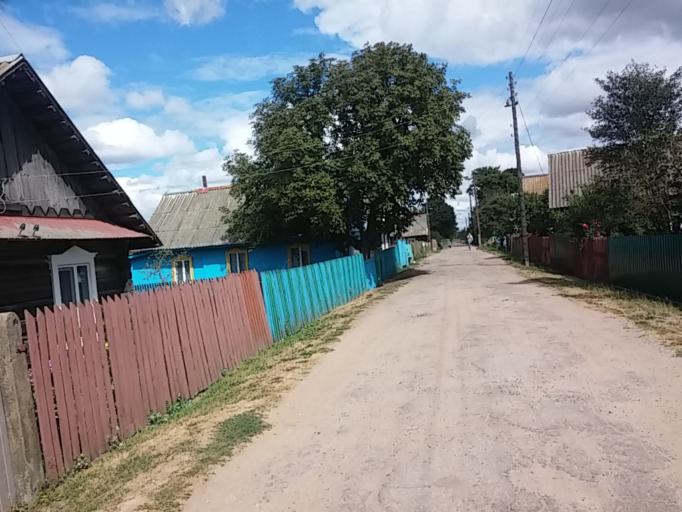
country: BY
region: Minsk
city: Chervyen'
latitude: 53.7789
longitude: 28.2677
